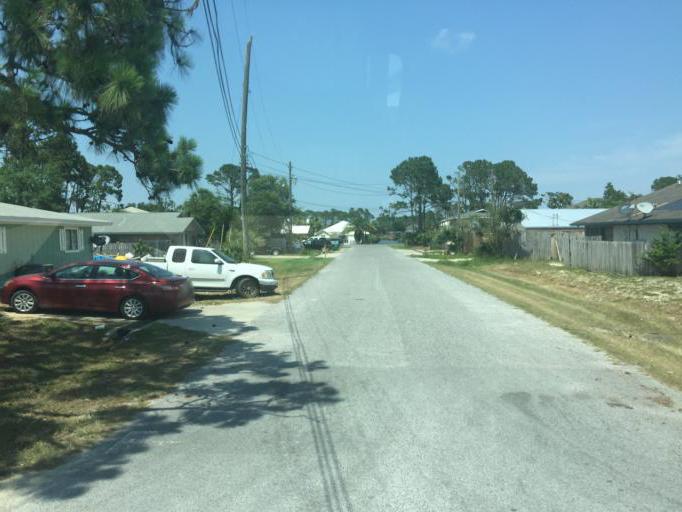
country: US
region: Florida
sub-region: Bay County
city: Lower Grand Lagoon
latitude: 30.1603
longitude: -85.7749
